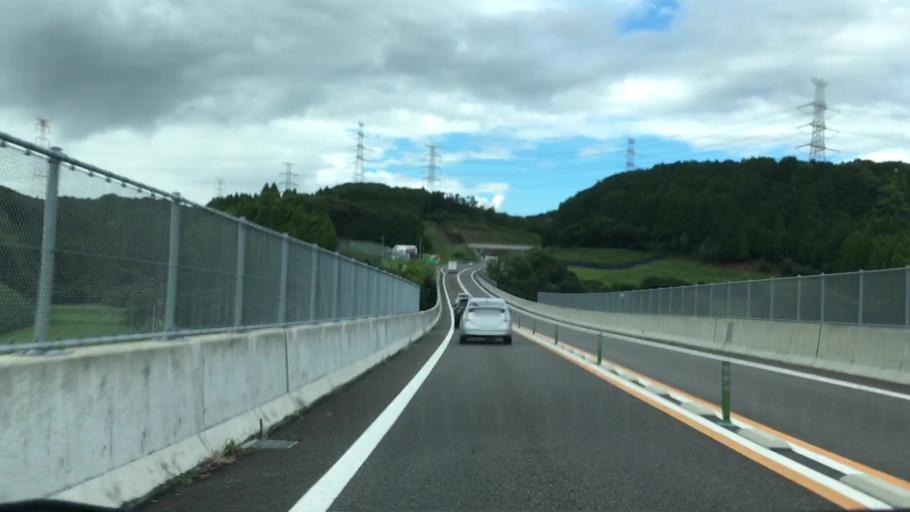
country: JP
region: Saga Prefecture
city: Imaricho-ko
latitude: 33.3476
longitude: 129.9247
